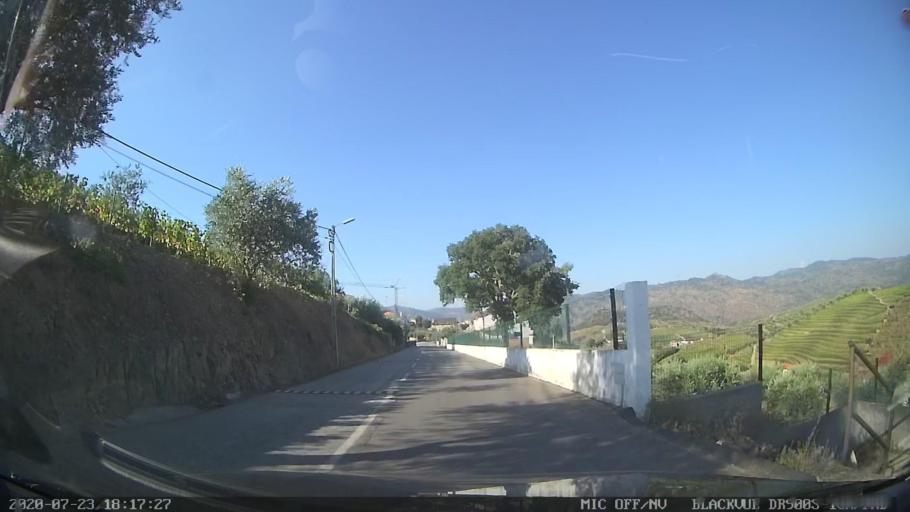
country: PT
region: Viseu
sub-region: Sao Joao da Pesqueira
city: Sao Joao da Pesqueira
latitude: 41.1825
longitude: -7.4158
